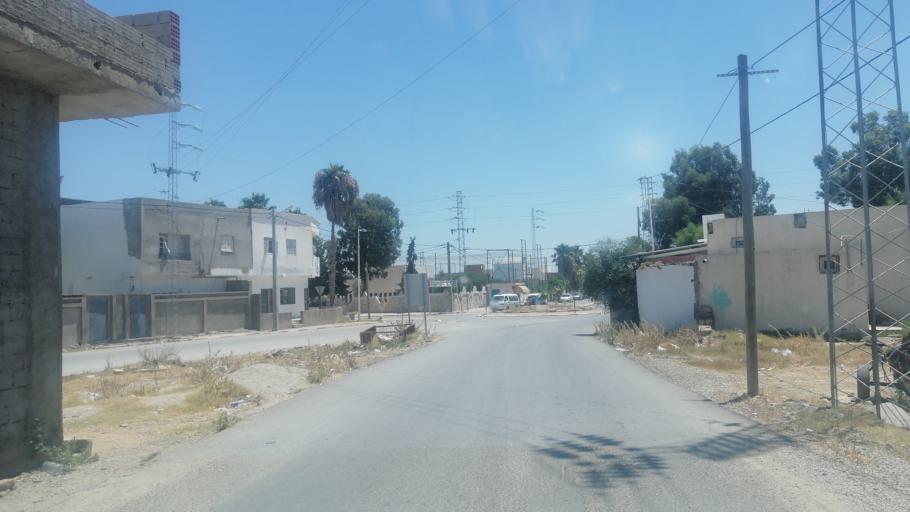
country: TN
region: Al Qayrawan
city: Sbikha
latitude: 36.1220
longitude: 10.0885
